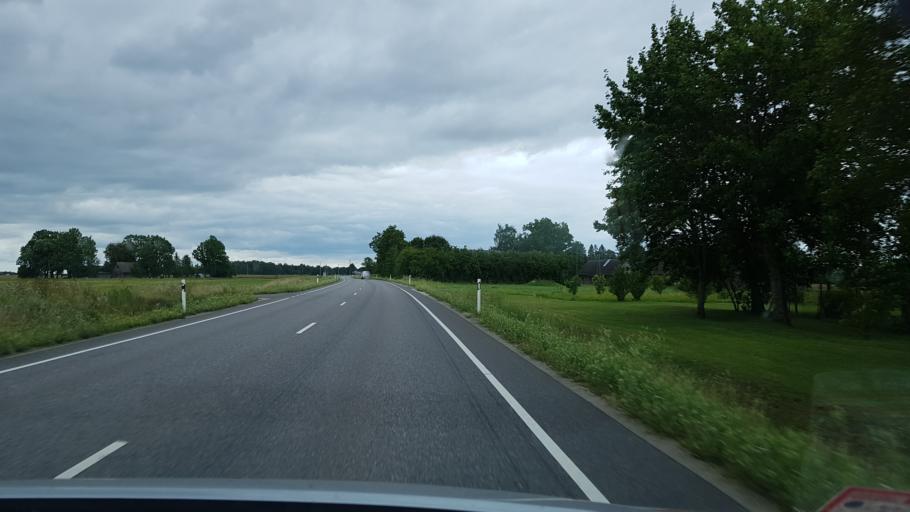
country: EE
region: Tartu
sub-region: Tartu linn
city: Tartu
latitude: 58.4213
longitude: 26.8666
